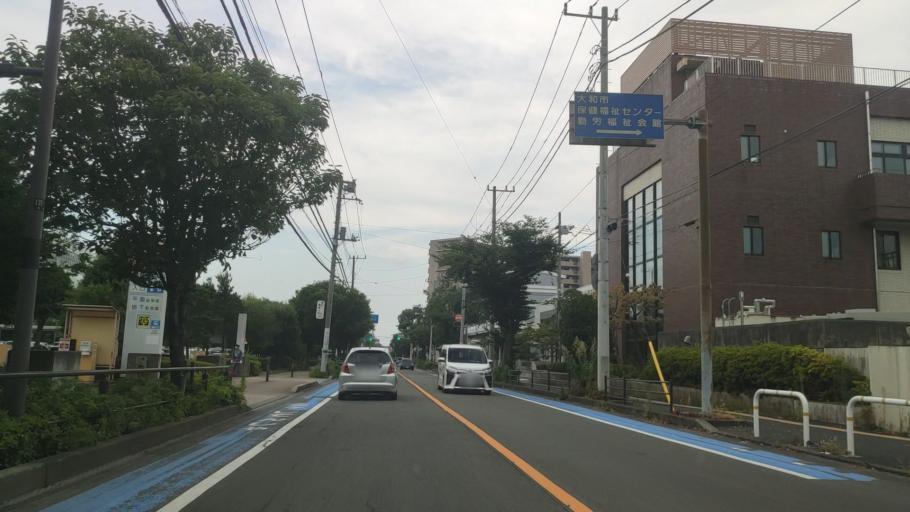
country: JP
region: Kanagawa
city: Minami-rinkan
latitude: 35.4905
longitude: 139.4556
